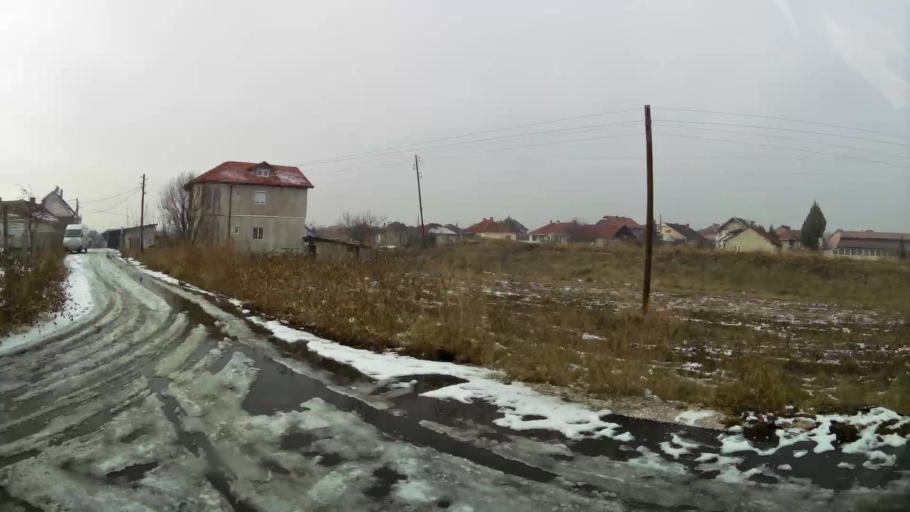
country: MK
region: Ilinden
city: Ilinden
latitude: 41.9942
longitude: 21.5843
